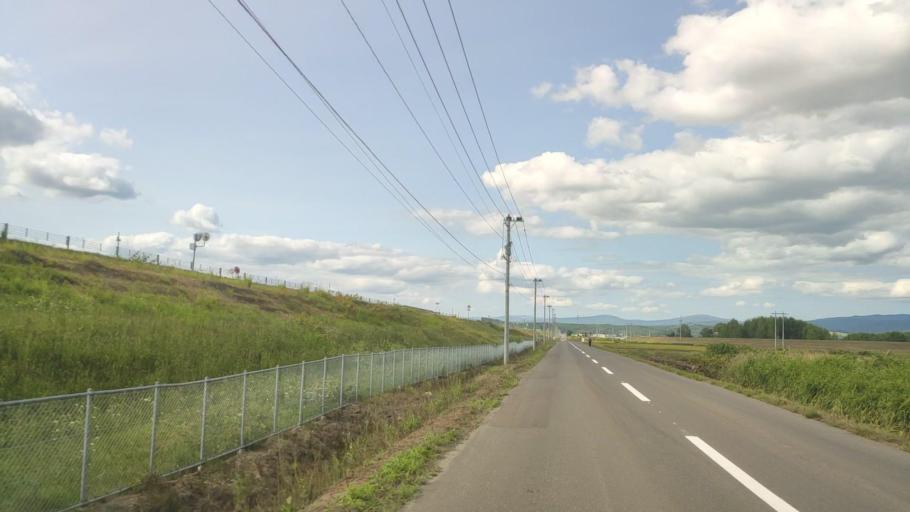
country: JP
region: Hokkaido
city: Nayoro
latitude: 44.3473
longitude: 142.4362
